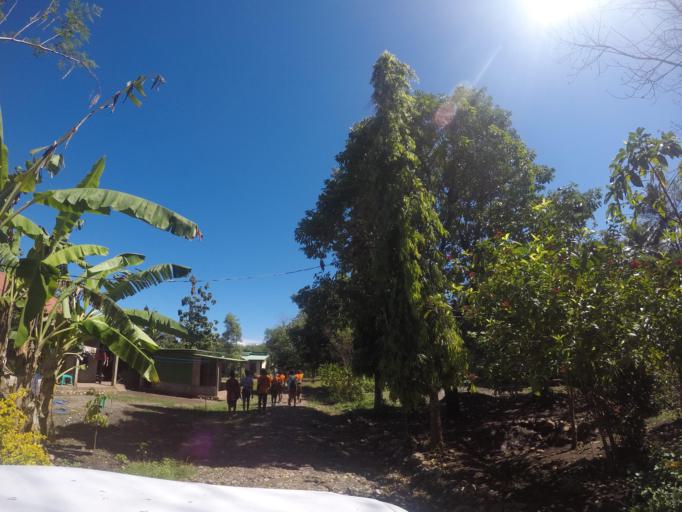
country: TL
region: Bobonaro
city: Maliana
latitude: -8.9893
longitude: 125.2042
